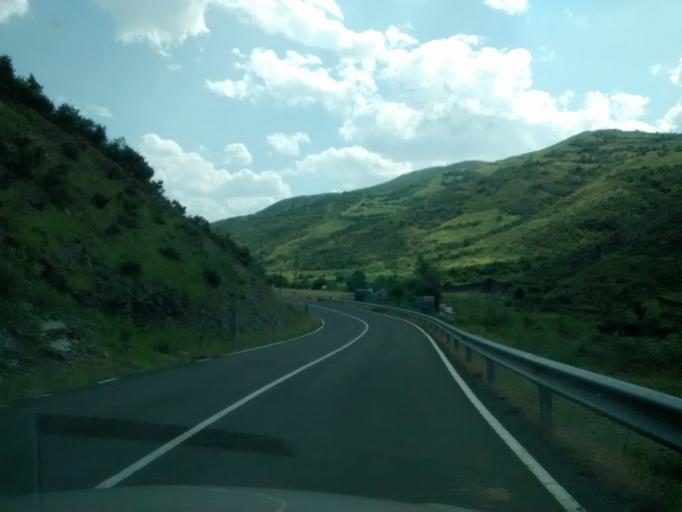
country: ES
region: La Rioja
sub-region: Provincia de La Rioja
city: Jalon de Cameros
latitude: 42.2106
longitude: -2.4779
